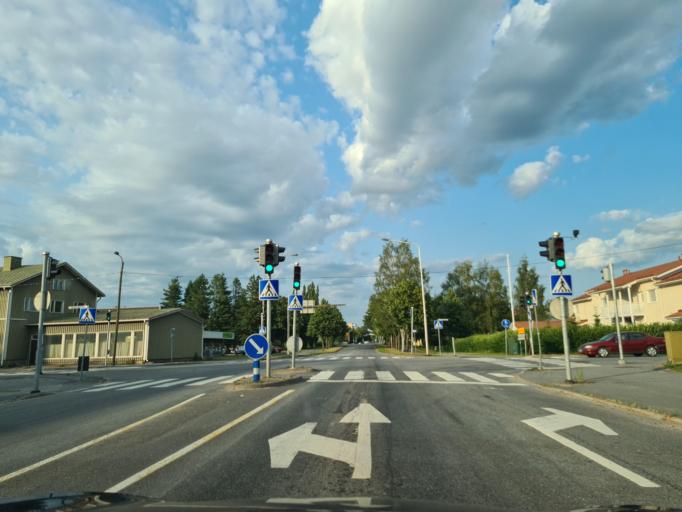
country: FI
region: Southern Ostrobothnia
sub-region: Seinaejoki
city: Lapua
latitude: 62.9701
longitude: 22.9964
